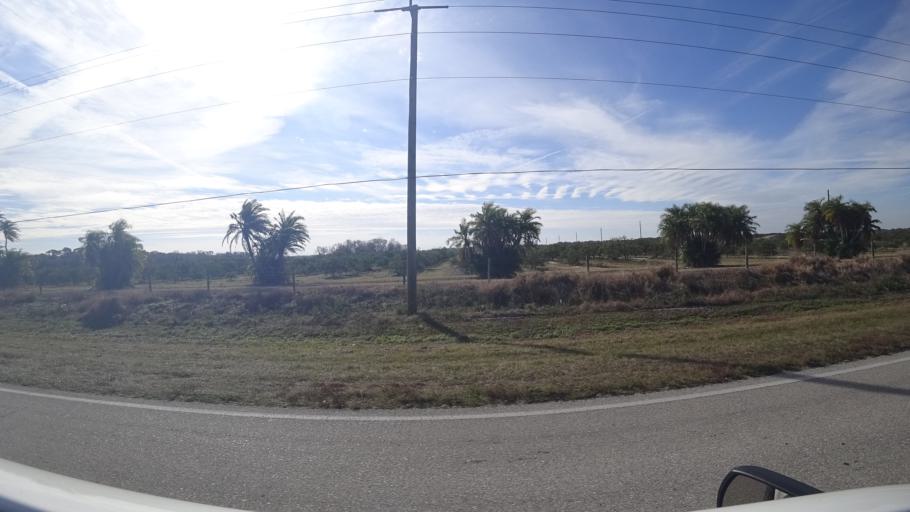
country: US
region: Florida
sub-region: Manatee County
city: Ellenton
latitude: 27.6012
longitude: -82.4773
